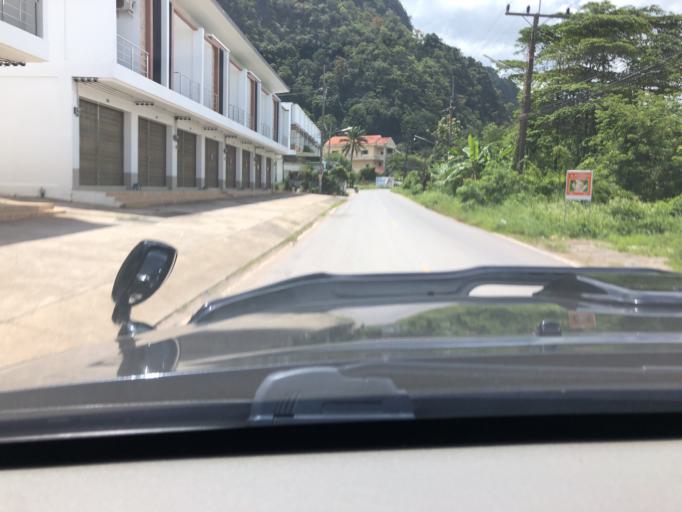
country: TH
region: Krabi
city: Krabi
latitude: 8.1197
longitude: 98.9241
